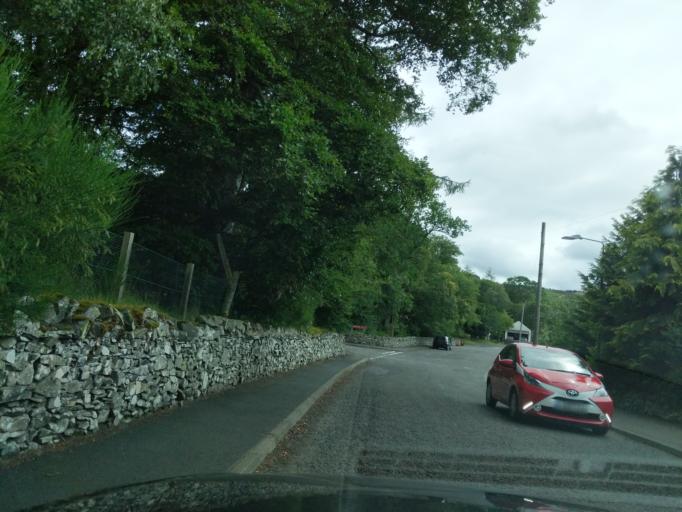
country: GB
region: Scotland
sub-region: The Scottish Borders
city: Peebles
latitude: 55.6450
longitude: -3.1990
